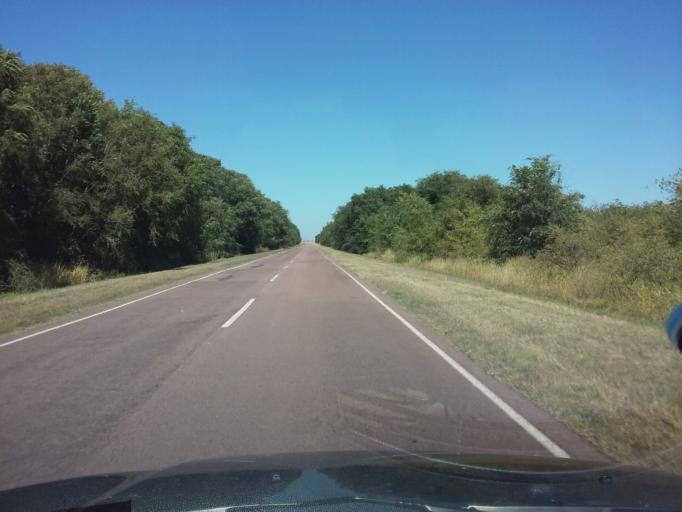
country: AR
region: La Pampa
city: Colonia Baron
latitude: -36.2356
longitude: -63.9427
